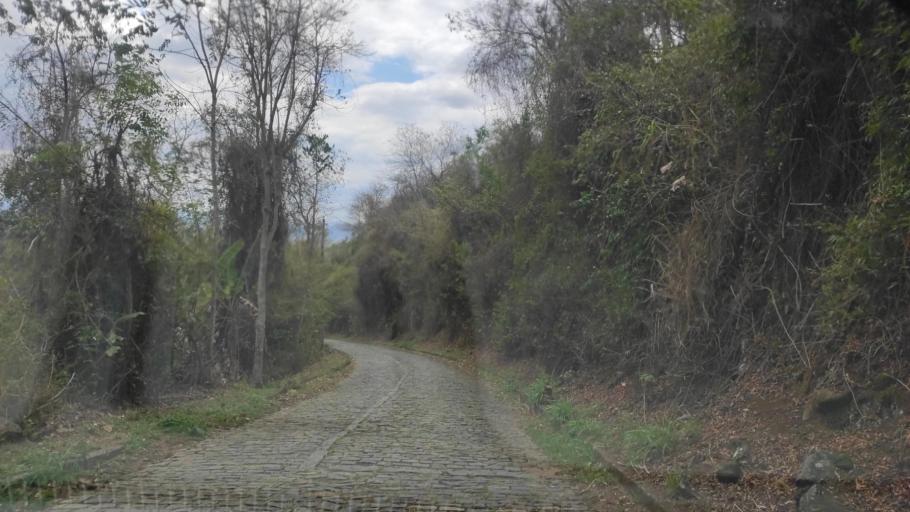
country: BR
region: Espirito Santo
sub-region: Vitoria
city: Vitoria
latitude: -20.2956
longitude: -40.3365
